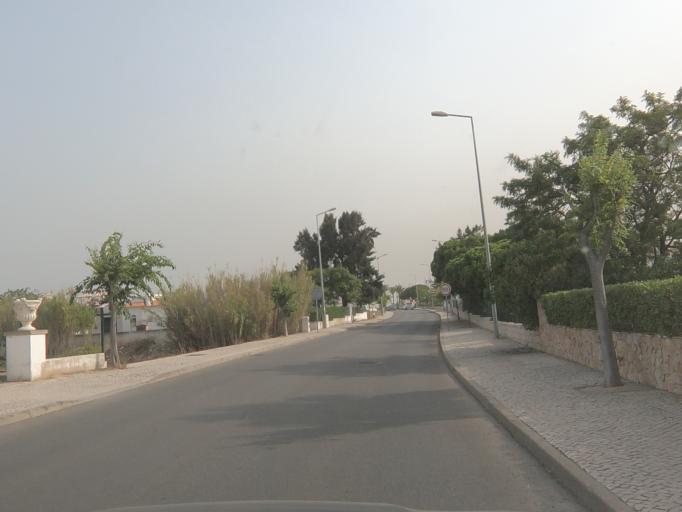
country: PT
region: Faro
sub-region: Albufeira
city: Guia
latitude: 37.0856
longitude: -8.3095
